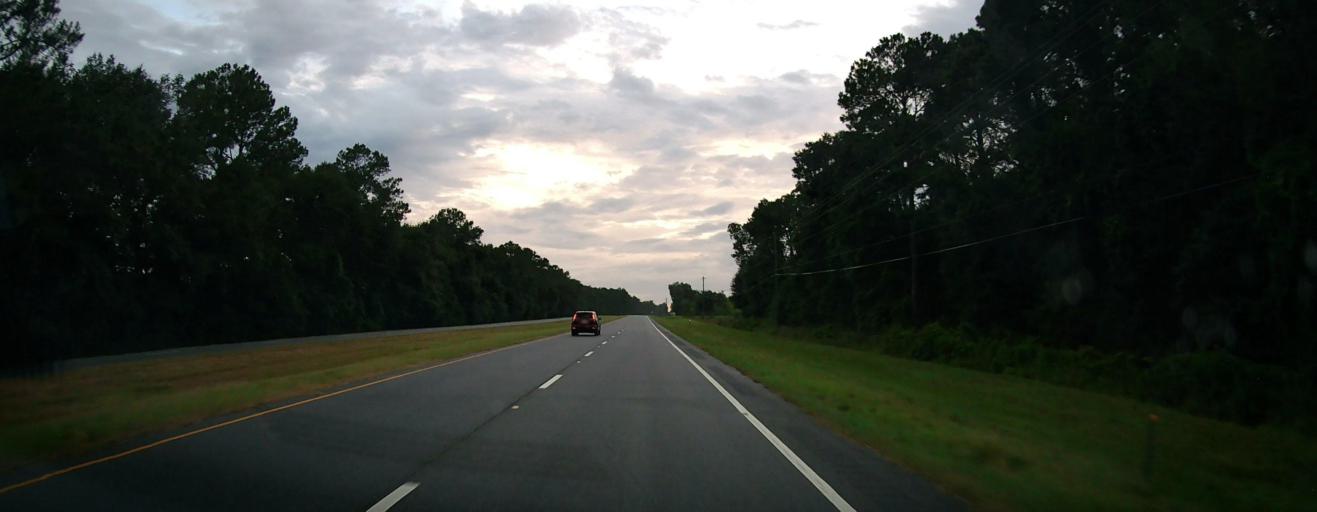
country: US
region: Georgia
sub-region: Lanier County
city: Lakeland
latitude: 30.9195
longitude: -83.0502
